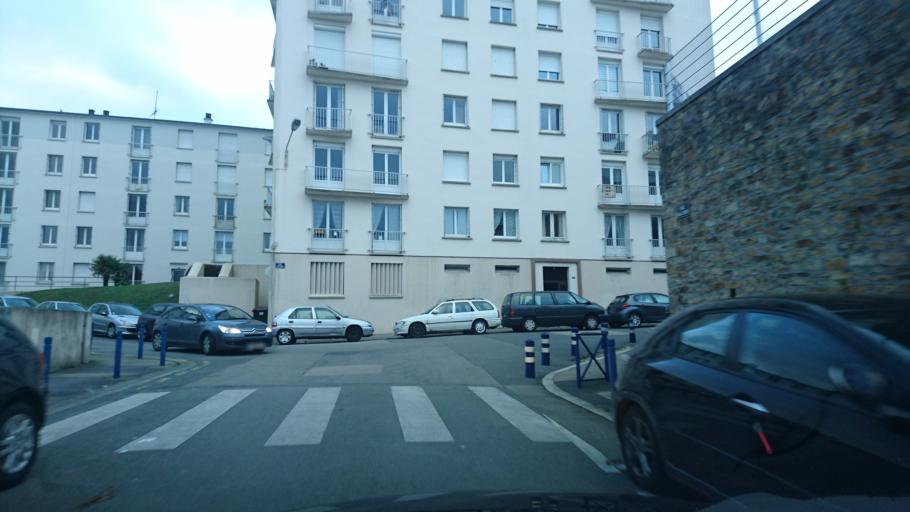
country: FR
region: Brittany
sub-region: Departement du Finistere
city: Brest
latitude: 48.3898
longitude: -4.4797
